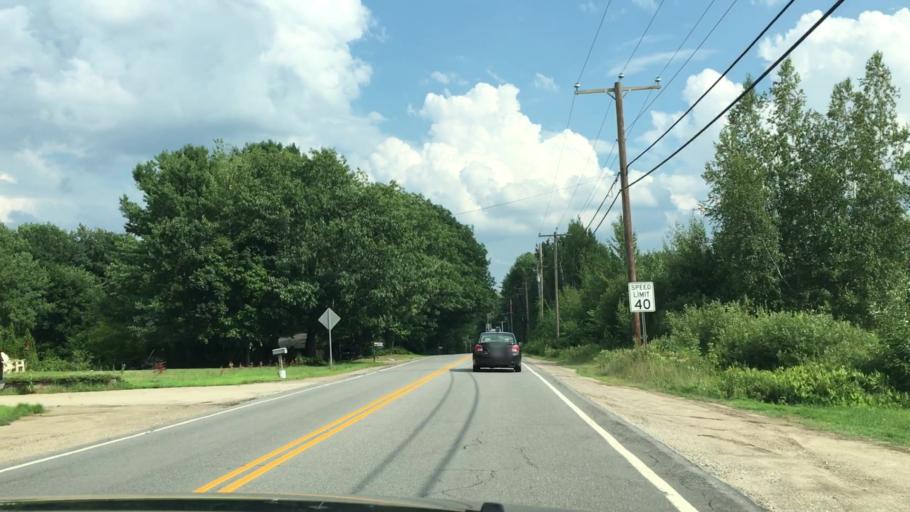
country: US
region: New Hampshire
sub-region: Belknap County
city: Gilford
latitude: 43.5880
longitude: -71.4206
